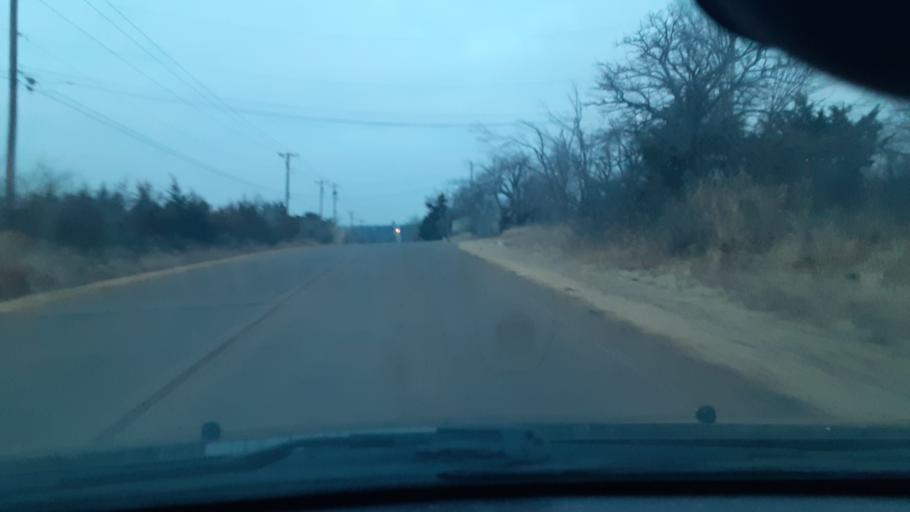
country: US
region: Oklahoma
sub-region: Logan County
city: Guthrie
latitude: 35.8623
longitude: -97.4076
